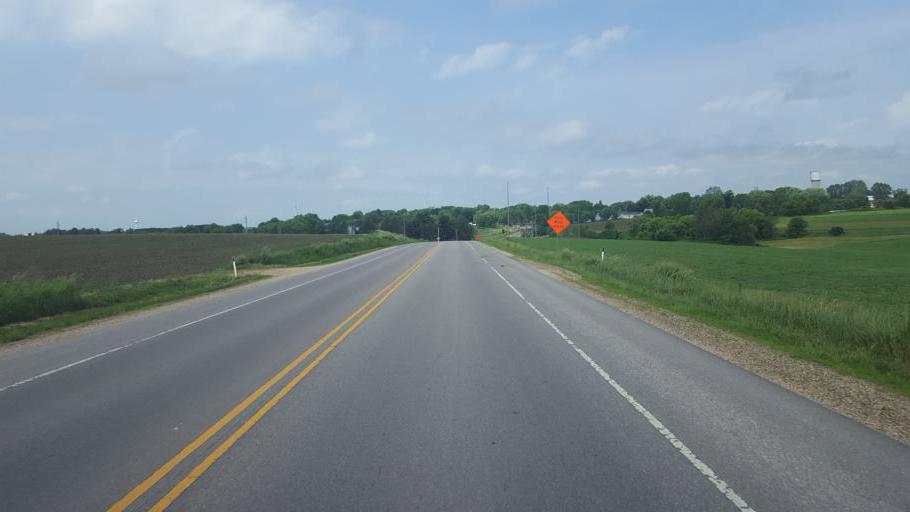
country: US
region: Wisconsin
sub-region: Monroe County
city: Cashton
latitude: 43.7402
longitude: -90.7662
